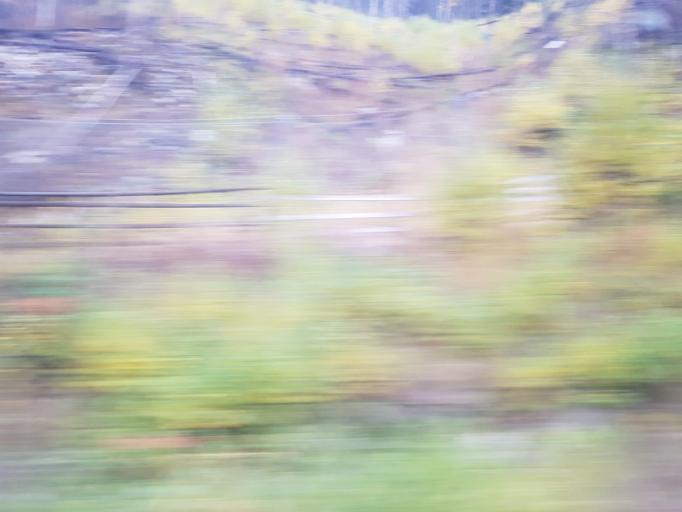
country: NO
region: Oppland
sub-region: Sel
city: Otta
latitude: 61.8548
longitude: 9.4161
